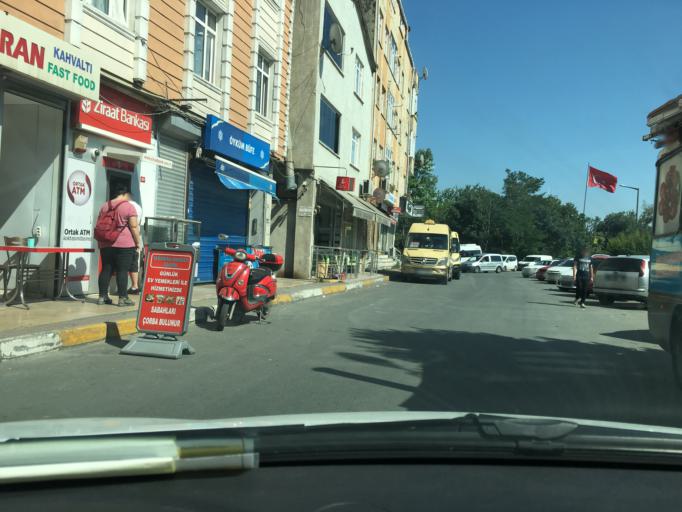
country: TR
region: Istanbul
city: Sisli
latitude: 41.0802
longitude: 28.9441
